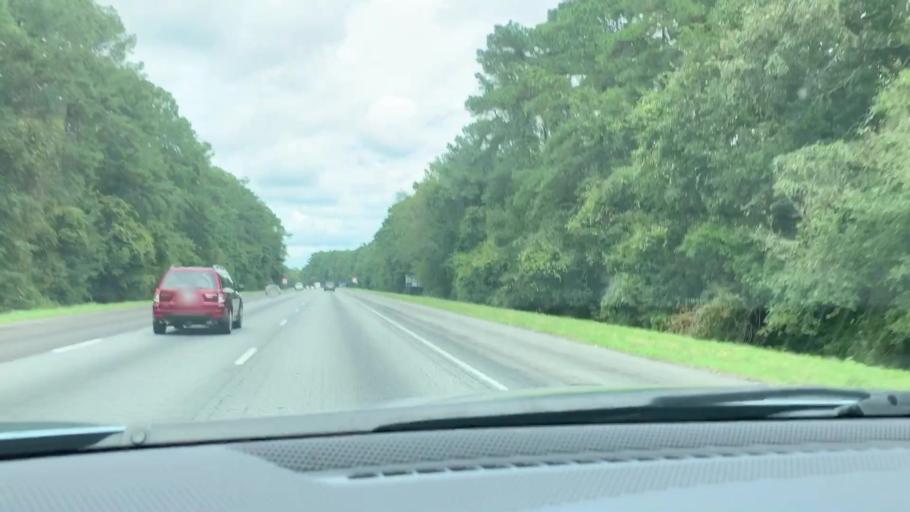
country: US
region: Georgia
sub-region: Bryan County
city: Richmond Hill
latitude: 31.8936
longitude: -81.3247
